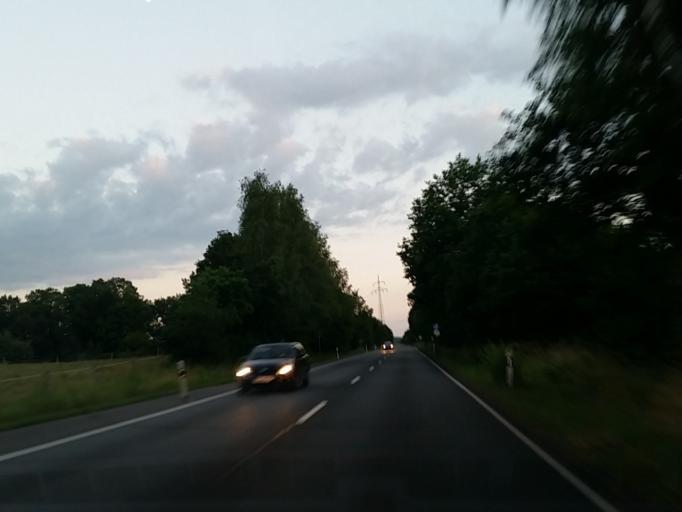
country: DE
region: Saarland
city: Wadern
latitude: 49.5257
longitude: 6.8758
